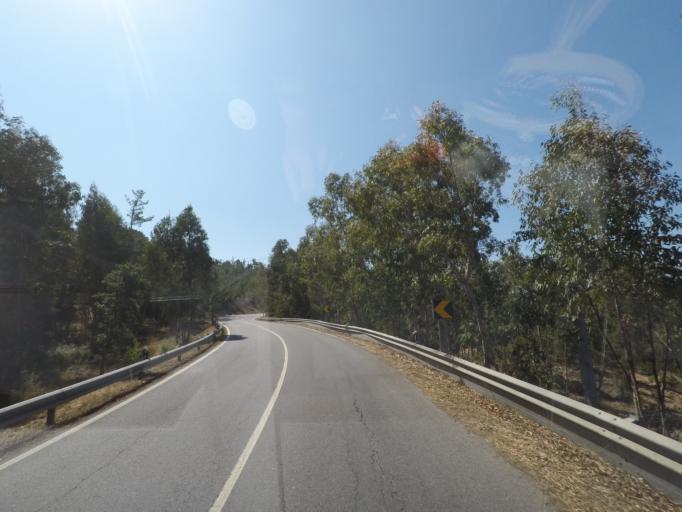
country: PT
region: Beja
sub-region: Odemira
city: Sao Teotonio
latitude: 37.5329
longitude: -8.6952
